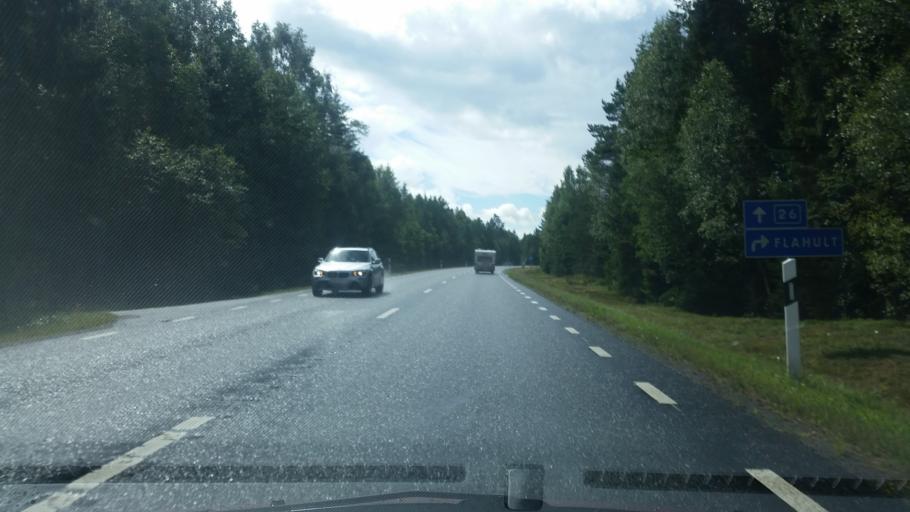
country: SE
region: Joenkoeping
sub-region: Gislaveds Kommun
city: Gislaved
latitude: 57.3903
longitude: 13.5890
